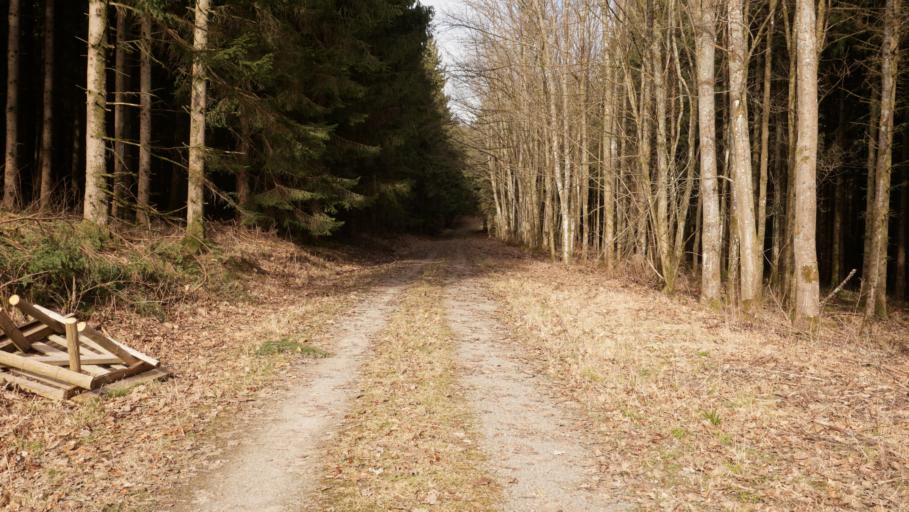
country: DE
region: Baden-Wuerttemberg
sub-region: Karlsruhe Region
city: Fahrenbach
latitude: 49.4510
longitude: 9.1241
